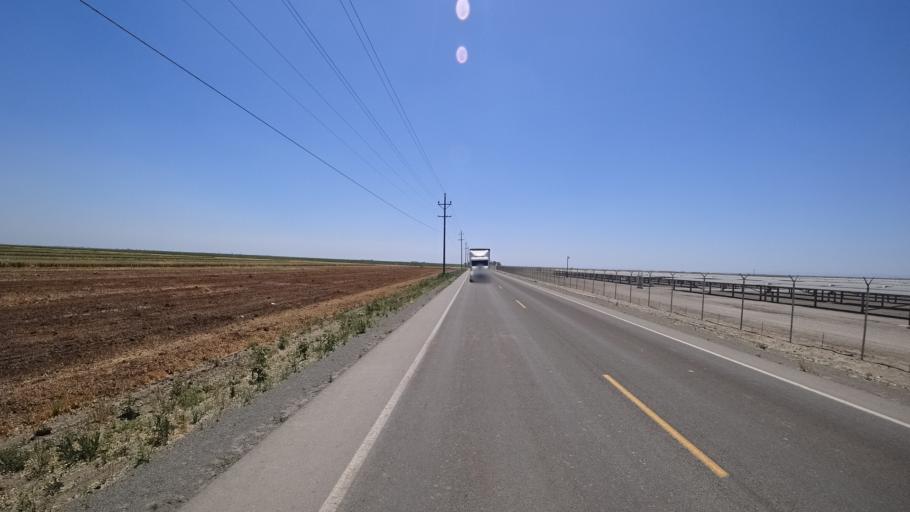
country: US
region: California
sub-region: Kings County
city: Corcoran
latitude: 36.1620
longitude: -119.6459
